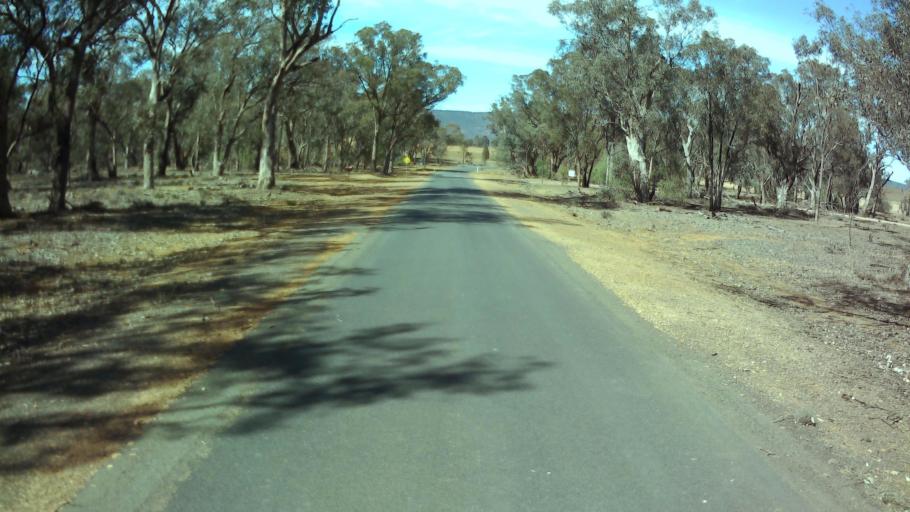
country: AU
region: New South Wales
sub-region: Weddin
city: Grenfell
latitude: -33.9386
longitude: 148.0798
